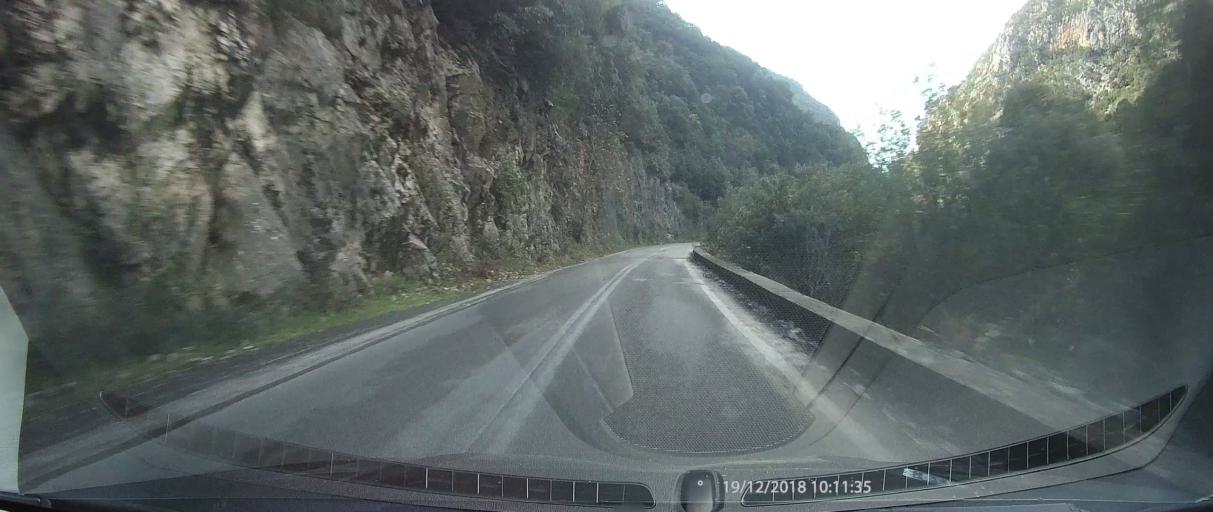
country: GR
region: Peloponnese
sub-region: Nomos Messinias
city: Kalamata
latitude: 37.0957
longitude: 22.1767
